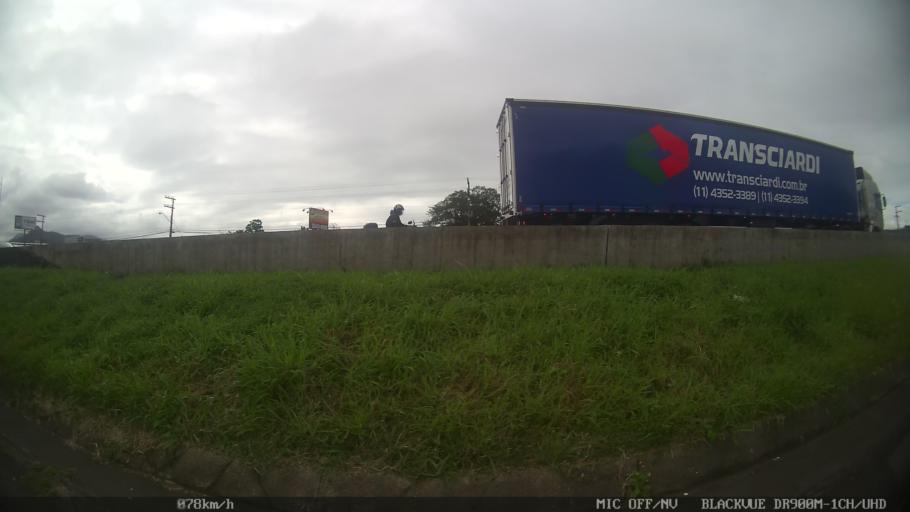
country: BR
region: Santa Catarina
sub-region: Biguacu
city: Biguacu
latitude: -27.5108
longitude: -48.6435
